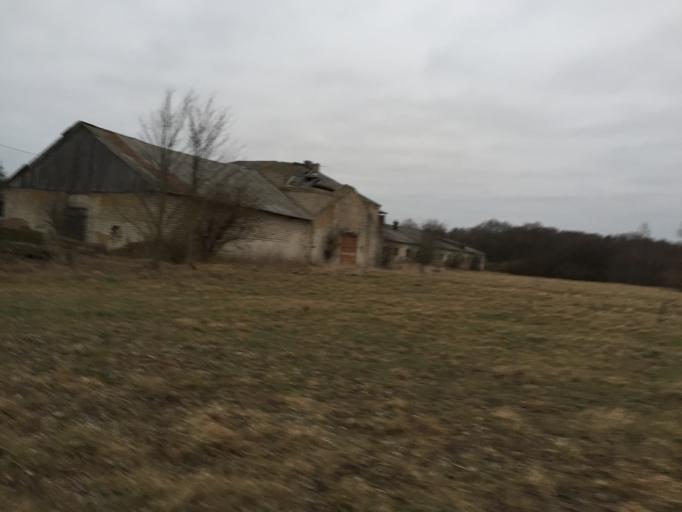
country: LT
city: Zagare
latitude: 56.3378
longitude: 23.2694
